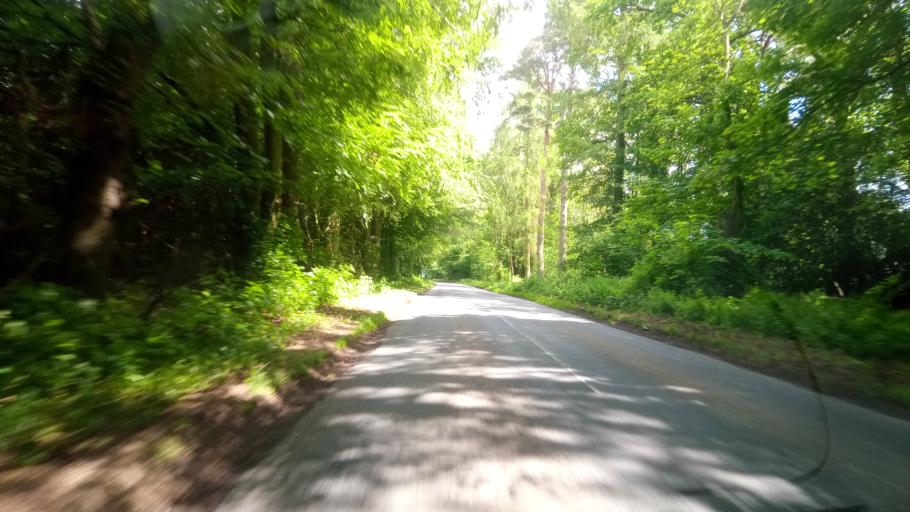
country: GB
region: Scotland
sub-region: The Scottish Borders
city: Kelso
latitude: 55.5792
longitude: -2.3961
